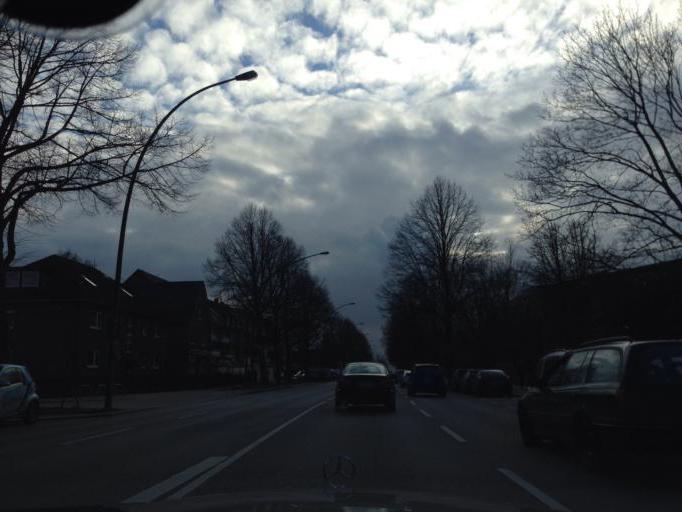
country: DE
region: Hamburg
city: Wandsbek
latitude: 53.5469
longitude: 10.1065
